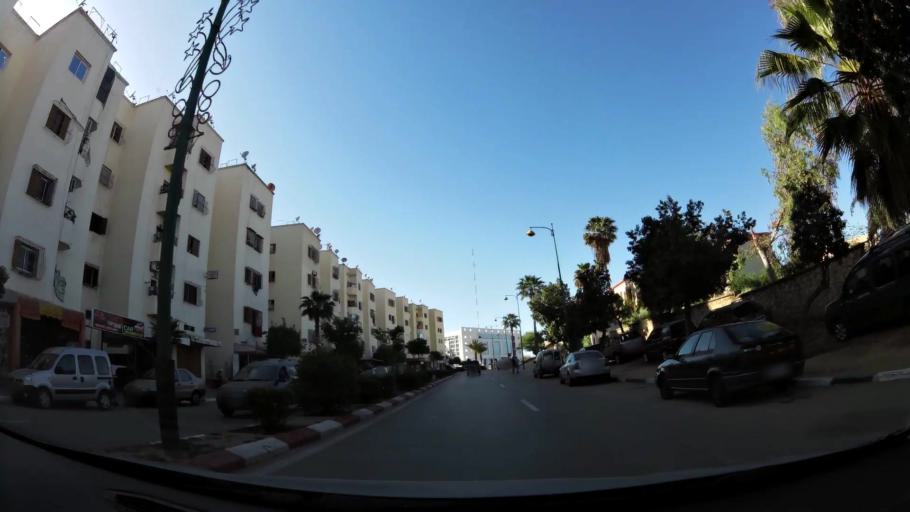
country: MA
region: Meknes-Tafilalet
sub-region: Meknes
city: Meknes
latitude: 33.8689
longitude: -5.5763
